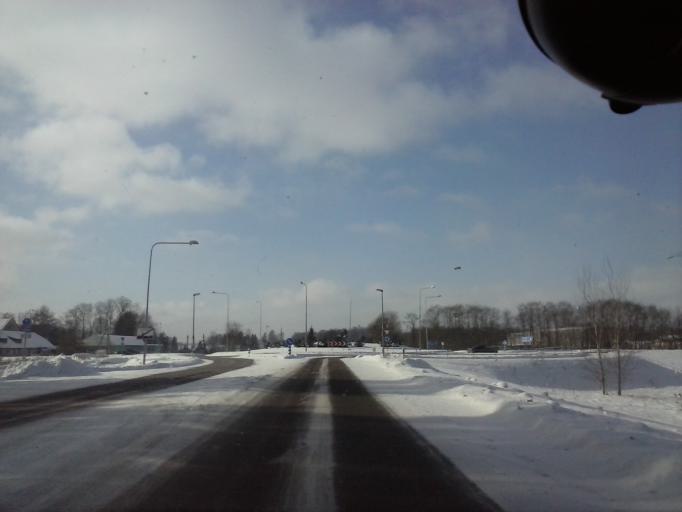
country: EE
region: Viljandimaa
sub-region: Viljandi linn
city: Viljandi
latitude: 58.3560
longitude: 25.5609
